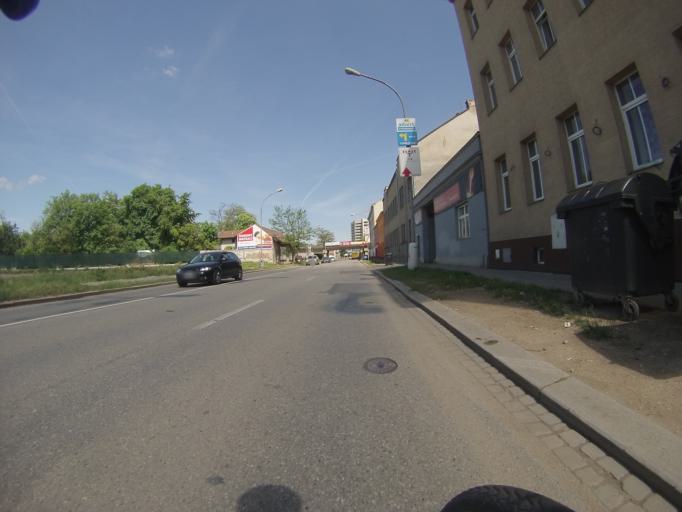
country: CZ
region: South Moravian
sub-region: Mesto Brno
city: Brno
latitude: 49.1839
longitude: 16.6191
